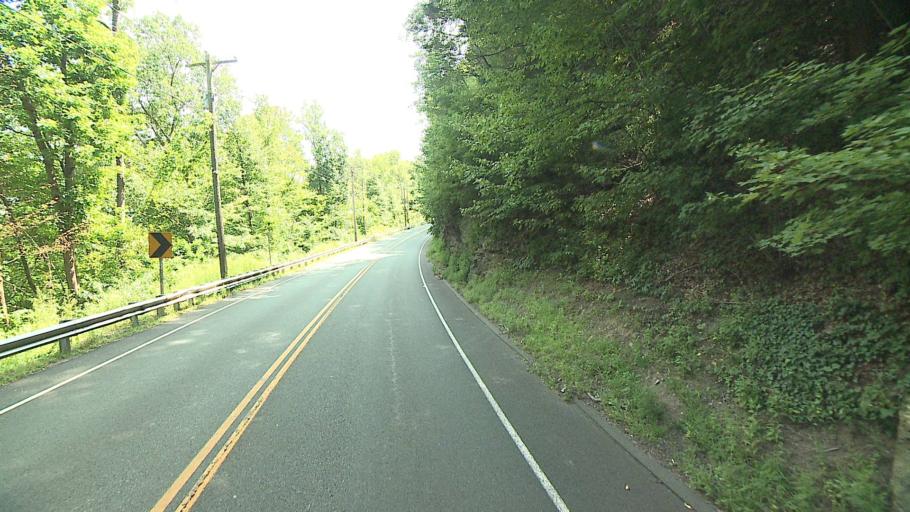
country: US
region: Connecticut
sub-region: Fairfield County
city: Shelton
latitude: 41.3361
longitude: -73.1234
